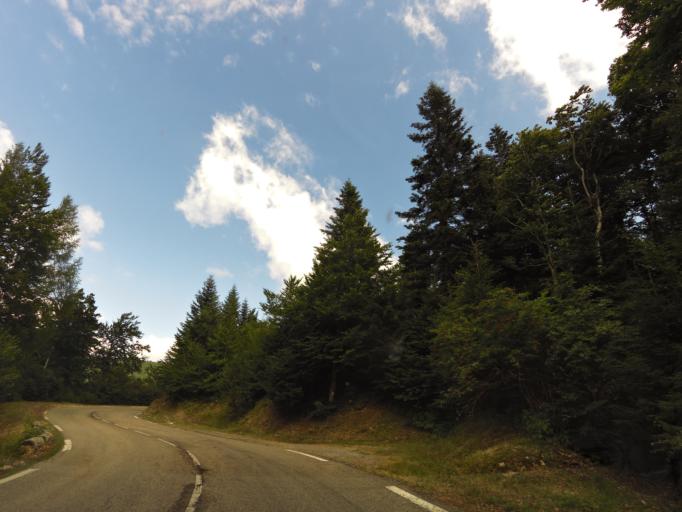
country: FR
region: Languedoc-Roussillon
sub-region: Departement du Gard
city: Valleraugue
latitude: 44.1025
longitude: 3.5318
